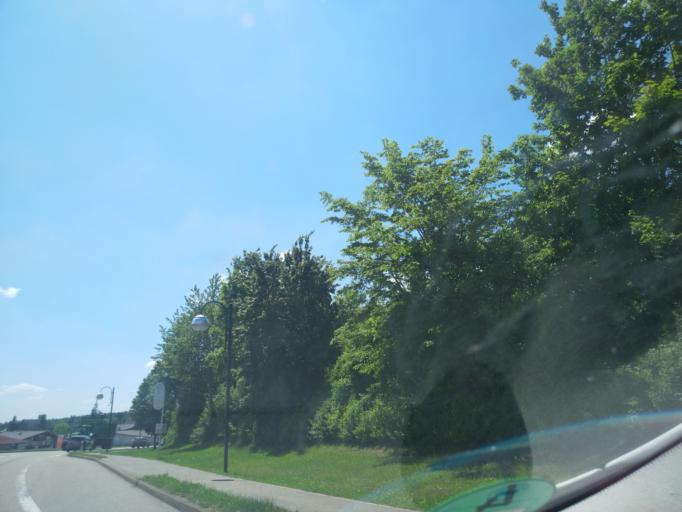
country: DE
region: Baden-Wuerttemberg
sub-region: Karlsruhe Region
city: Lossburg
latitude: 48.4226
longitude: 8.4461
